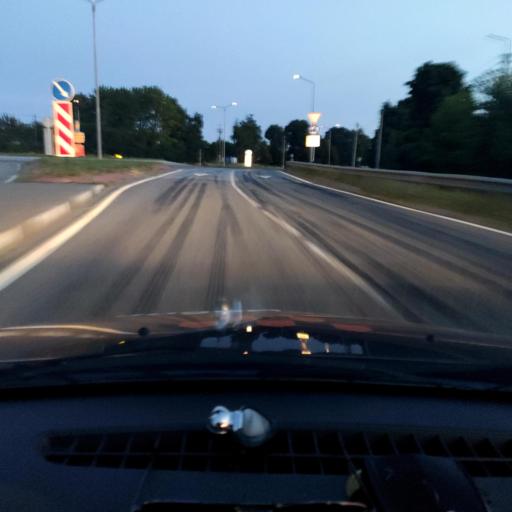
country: RU
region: Belgorod
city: Gubkin
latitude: 51.2782
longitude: 37.5937
